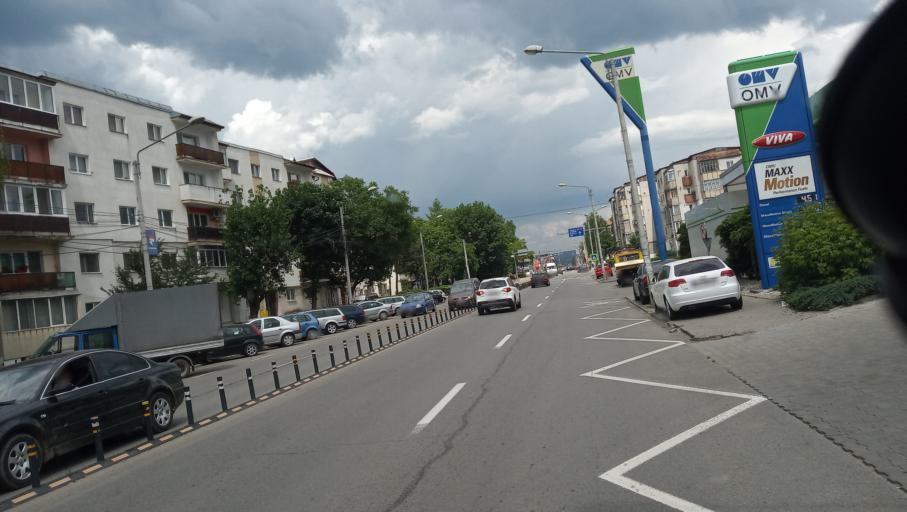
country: RO
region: Bistrita-Nasaud
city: Bistrita
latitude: 47.1413
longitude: 24.5068
